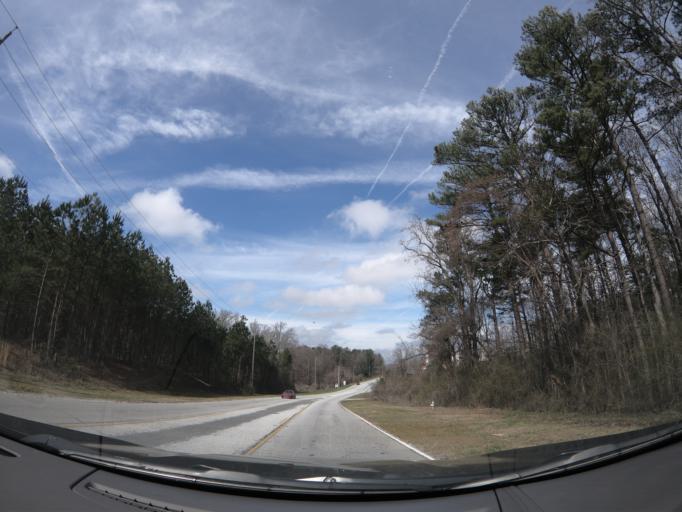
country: US
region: Georgia
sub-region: Fulton County
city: College Park
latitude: 33.6362
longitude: -84.4680
